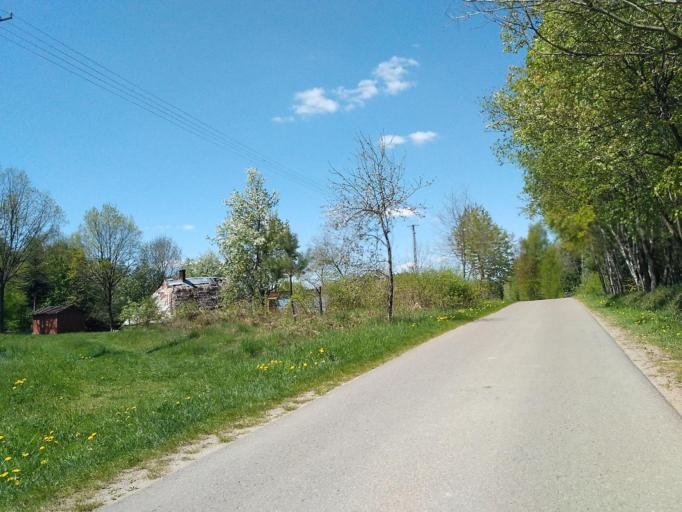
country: PL
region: Subcarpathian Voivodeship
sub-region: Powiat krosnienski
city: Korczyna
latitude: 49.7358
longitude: 21.8471
